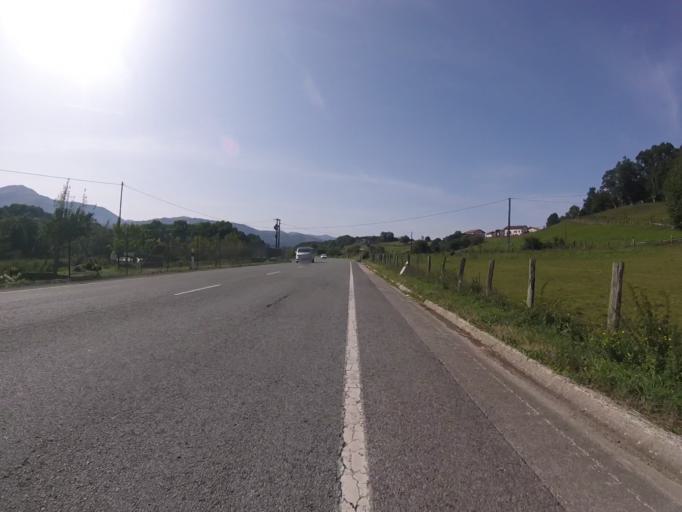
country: ES
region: Navarre
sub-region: Provincia de Navarra
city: Zugarramurdi
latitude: 43.1915
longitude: -1.4865
